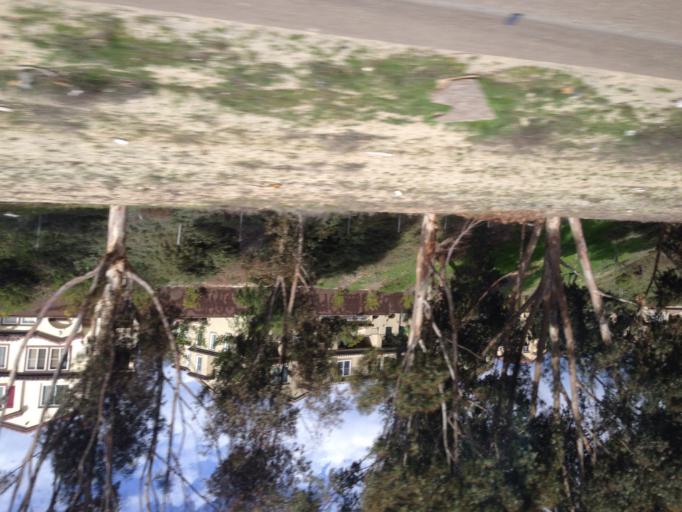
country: MX
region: Baja California
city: Tijuana
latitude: 32.5698
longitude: -117.0386
